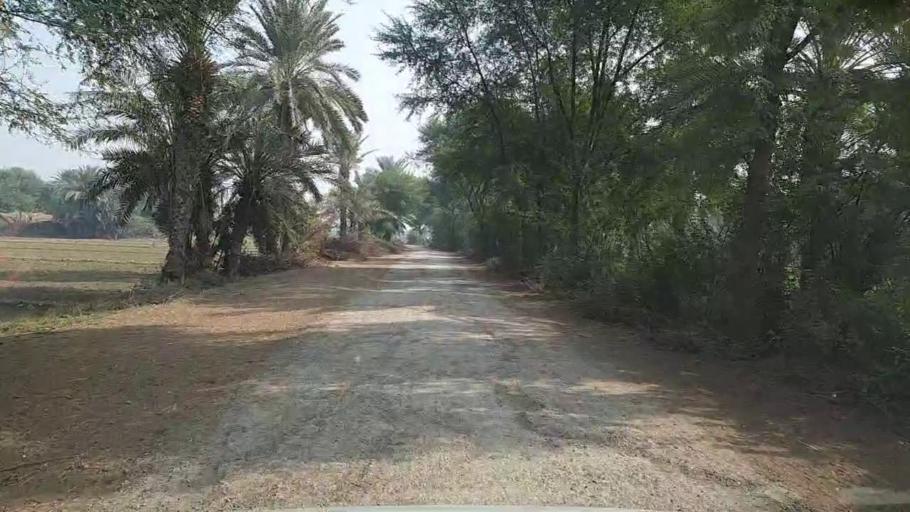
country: PK
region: Sindh
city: Setharja Old
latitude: 27.1387
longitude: 68.5075
